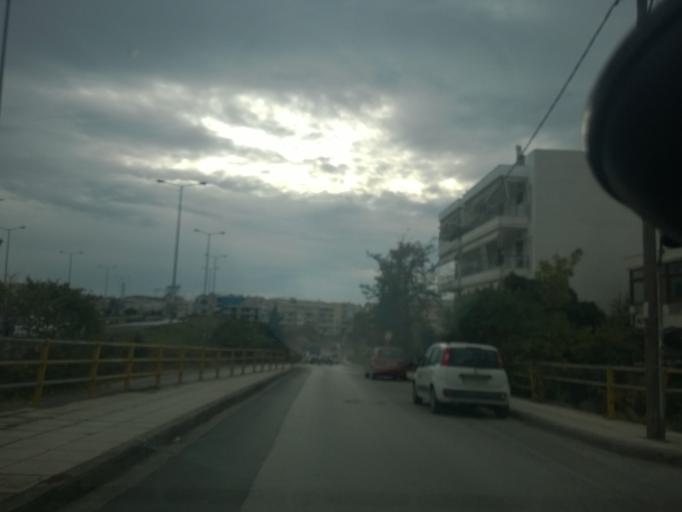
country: GR
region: Central Macedonia
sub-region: Nomos Thessalonikis
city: Kalamaria
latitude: 40.5935
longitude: 22.9650
